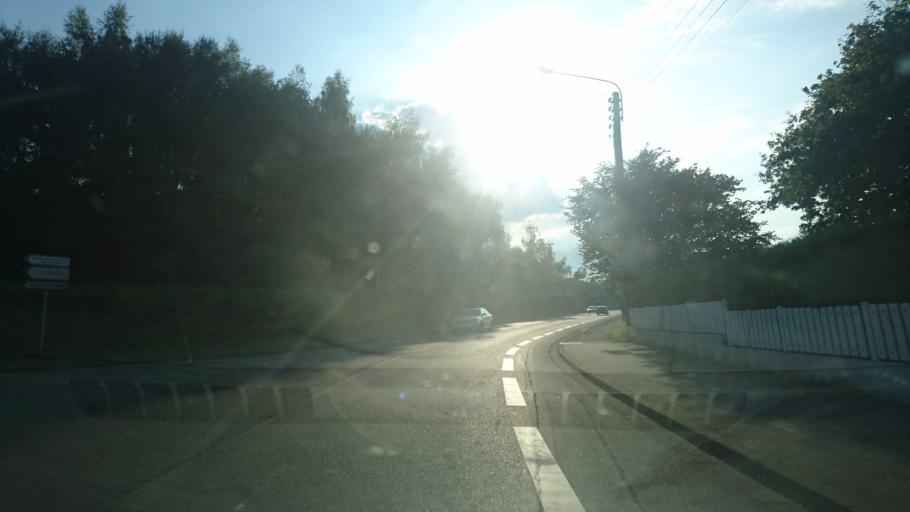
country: FR
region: Brittany
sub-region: Departement d'Ille-et-Vilaine
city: Redon
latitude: 47.6592
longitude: -2.0797
